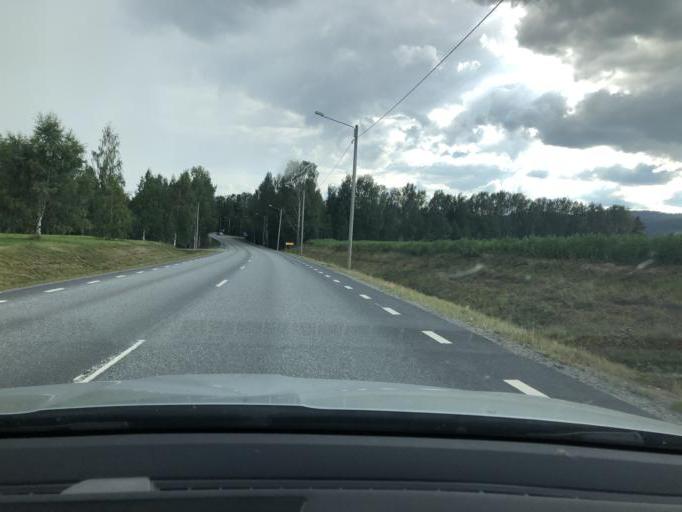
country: SE
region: Vaesternorrland
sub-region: Solleftea Kommun
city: Solleftea
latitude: 63.2437
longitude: 17.2074
